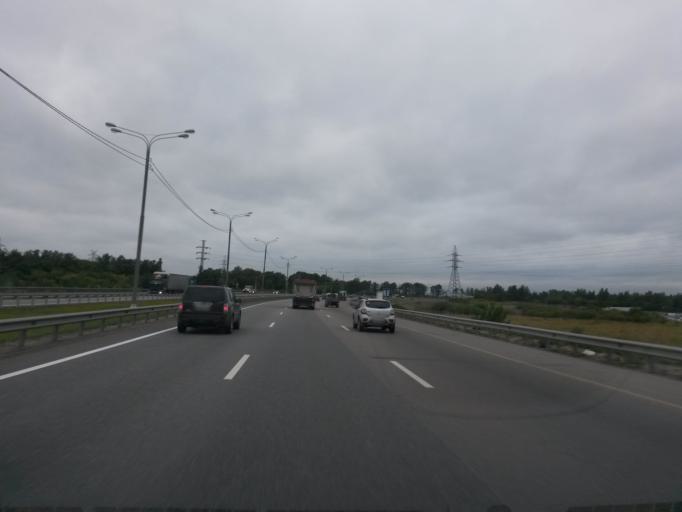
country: RU
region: Moskovskaya
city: Domodedovo
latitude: 55.4615
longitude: 37.7637
